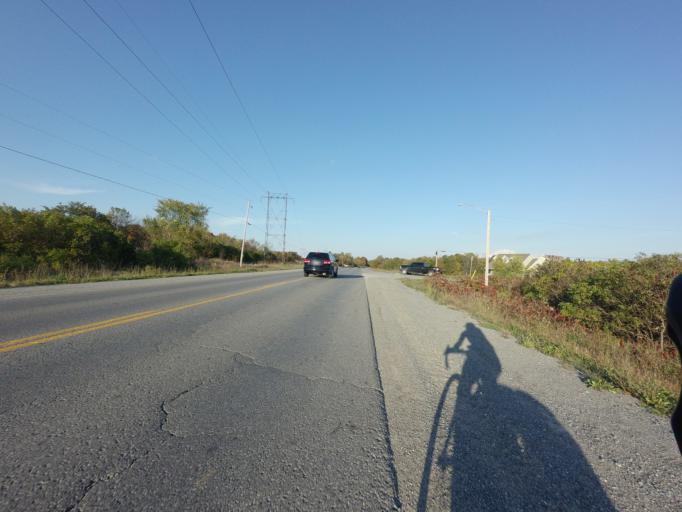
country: CA
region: Ontario
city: Kingston
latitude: 44.3561
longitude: -76.4307
